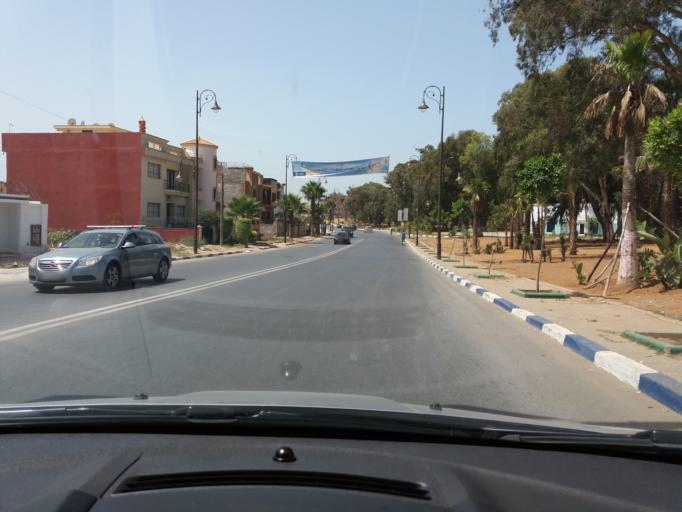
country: MA
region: Gharb-Chrarda-Beni Hssen
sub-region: Kenitra Province
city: Kenitra
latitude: 34.2700
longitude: -6.6407
